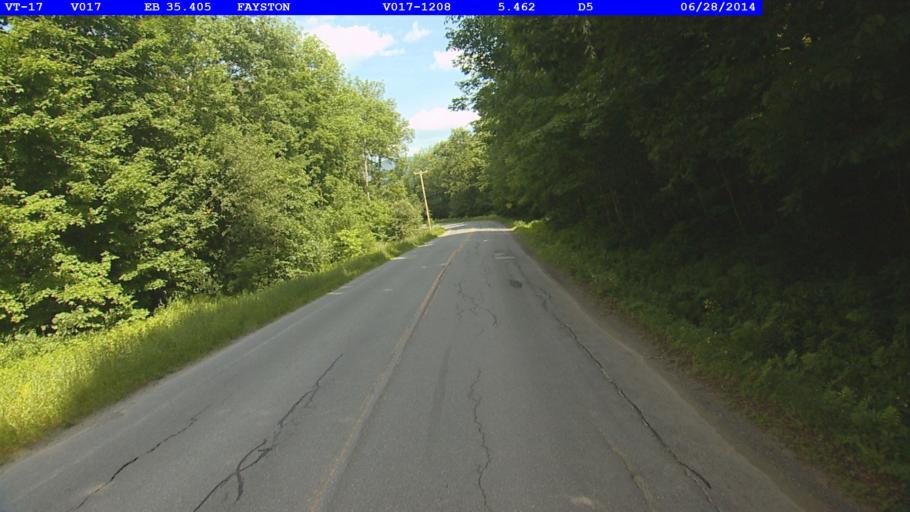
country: US
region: Vermont
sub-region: Washington County
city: Waterbury
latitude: 44.1829
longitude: -72.8500
